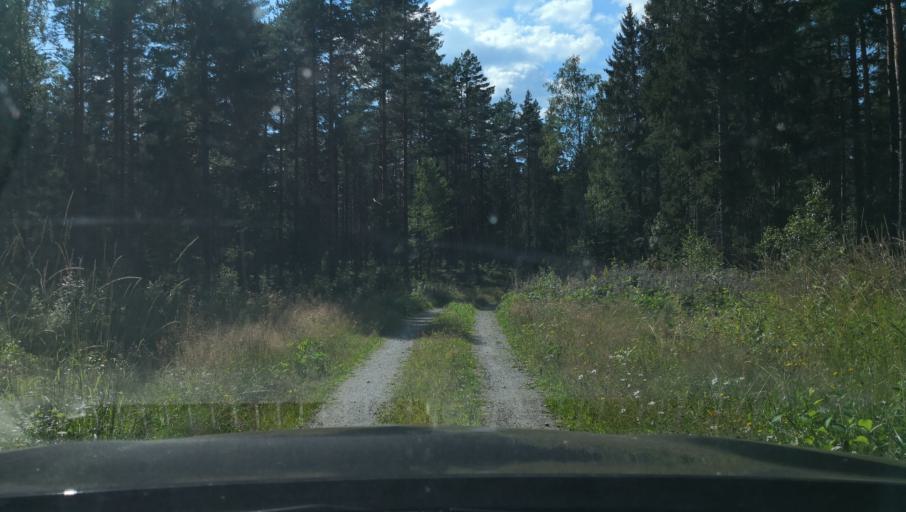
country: SE
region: Vaestmanland
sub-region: Vasteras
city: Skultuna
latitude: 59.7140
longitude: 16.3648
